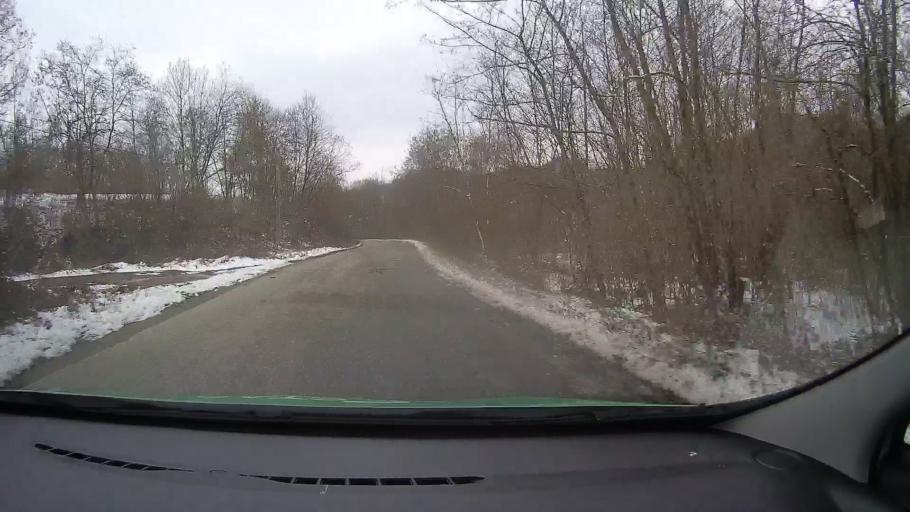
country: RO
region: Hunedoara
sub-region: Comuna Balsa
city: Balsa
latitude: 46.0399
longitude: 23.0743
